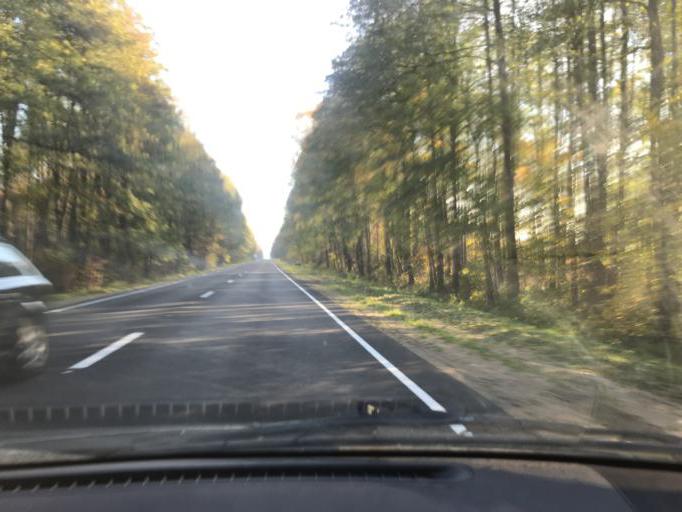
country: BY
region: Brest
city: Baranovichi
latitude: 52.8848
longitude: 25.7910
